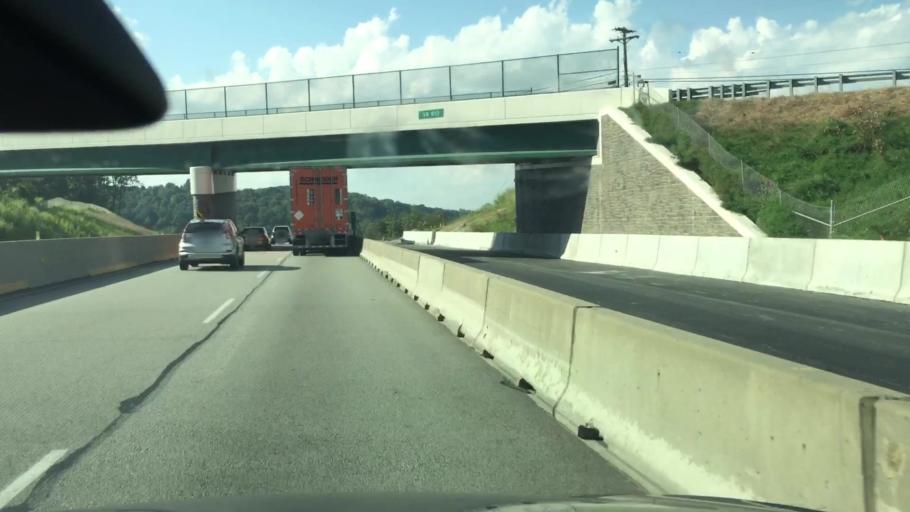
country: US
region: Pennsylvania
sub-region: Allegheny County
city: Russellton
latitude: 40.5828
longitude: -79.8720
